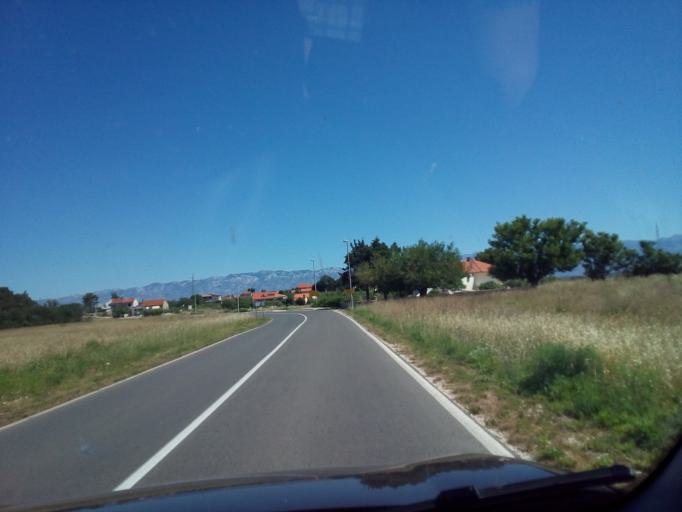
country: HR
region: Zadarska
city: Nin
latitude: 44.2336
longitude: 15.1818
